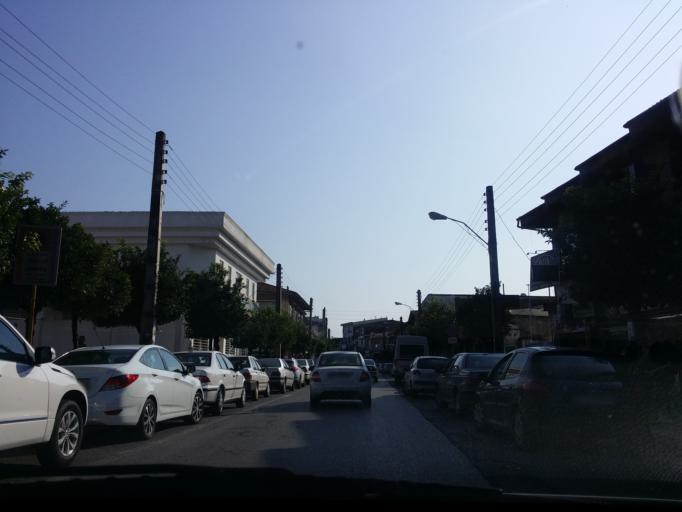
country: IR
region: Mazandaran
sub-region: Nowshahr
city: Nowshahr
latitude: 36.6508
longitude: 51.5020
